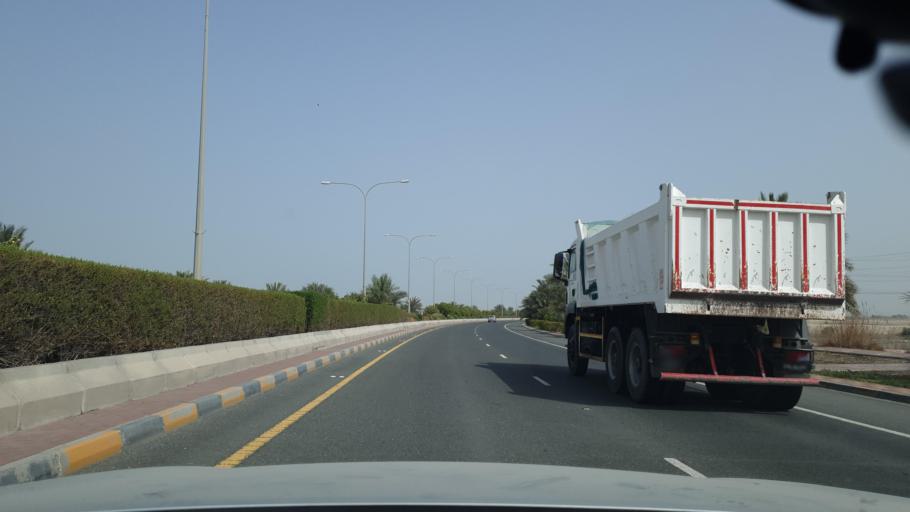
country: QA
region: Al Wakrah
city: Umm Sa'id
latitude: 25.0100
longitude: 51.5572
